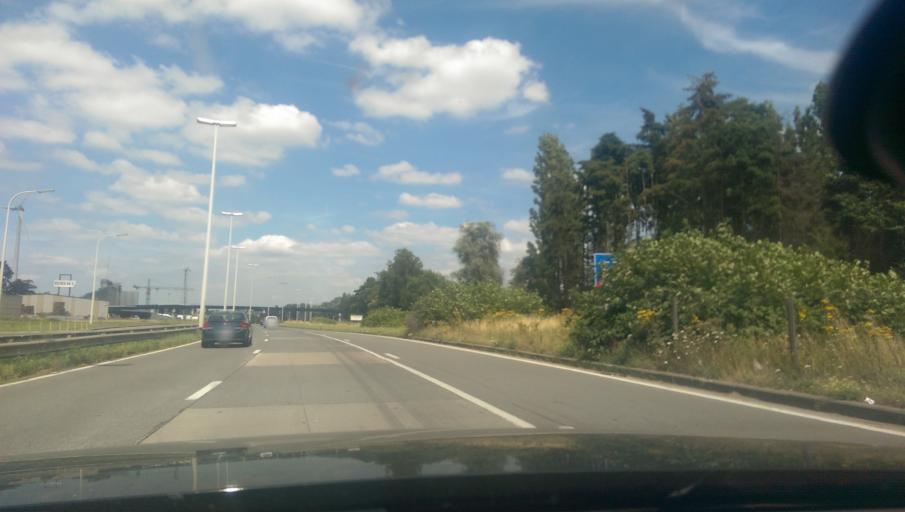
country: BE
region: Flanders
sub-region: Provincie Oost-Vlaanderen
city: Ledeberg
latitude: 51.0785
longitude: 3.7503
